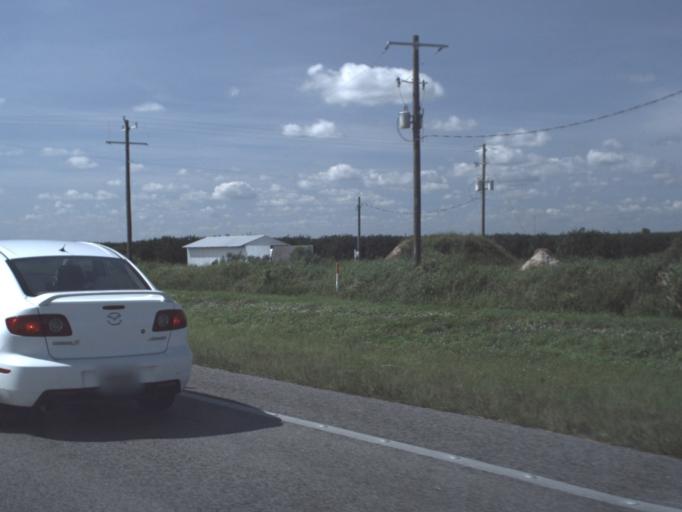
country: US
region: Florida
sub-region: Glades County
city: Moore Haven
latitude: 26.7535
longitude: -81.0899
